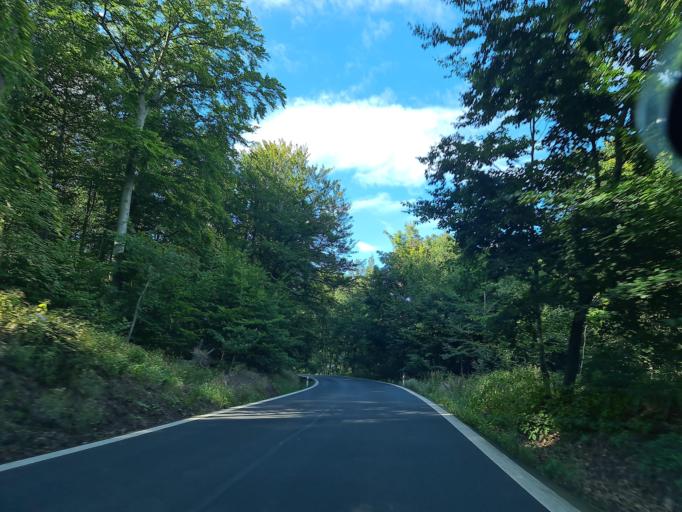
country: CZ
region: Ustecky
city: Mezibori
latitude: 50.6075
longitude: 13.5827
